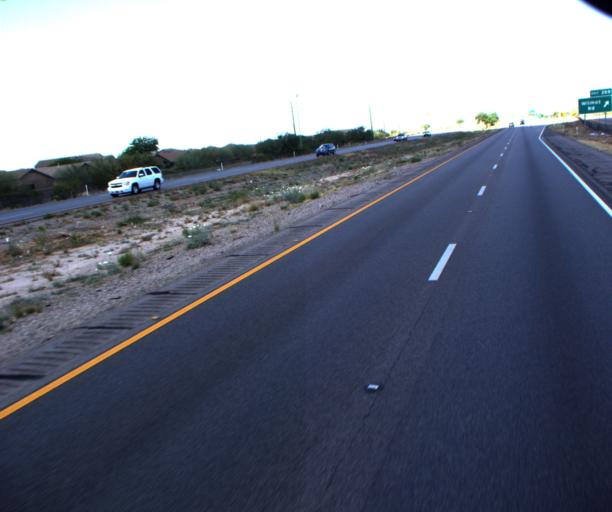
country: US
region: Arizona
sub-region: Pima County
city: Summit
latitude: 32.1111
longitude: -110.8523
